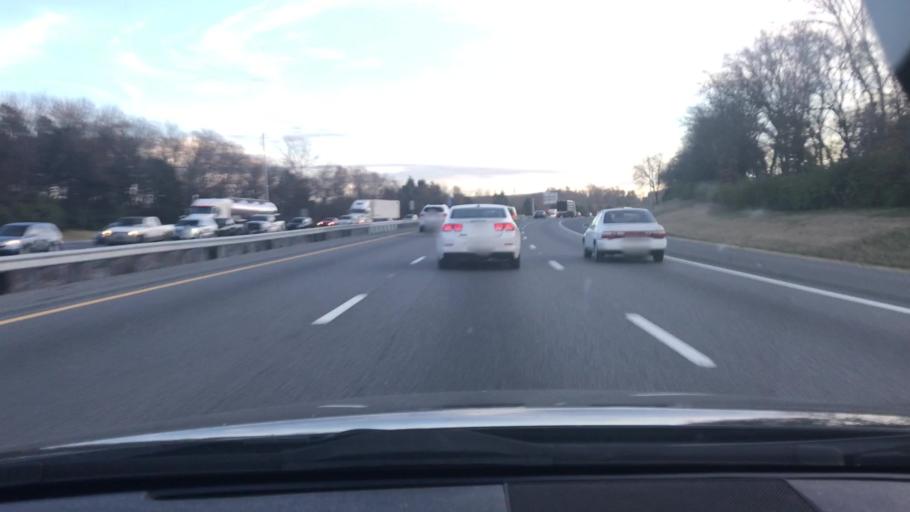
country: US
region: Tennessee
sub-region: Davidson County
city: Goodlettsville
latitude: 36.3170
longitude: -86.7018
